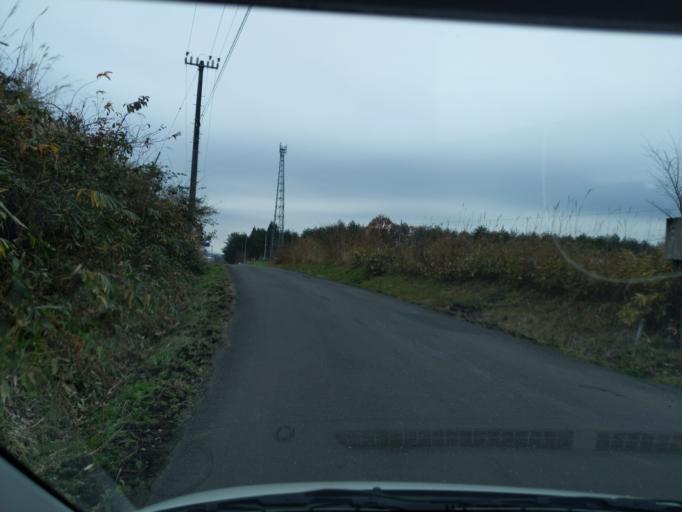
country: JP
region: Iwate
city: Ichinoseki
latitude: 38.9955
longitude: 141.0259
